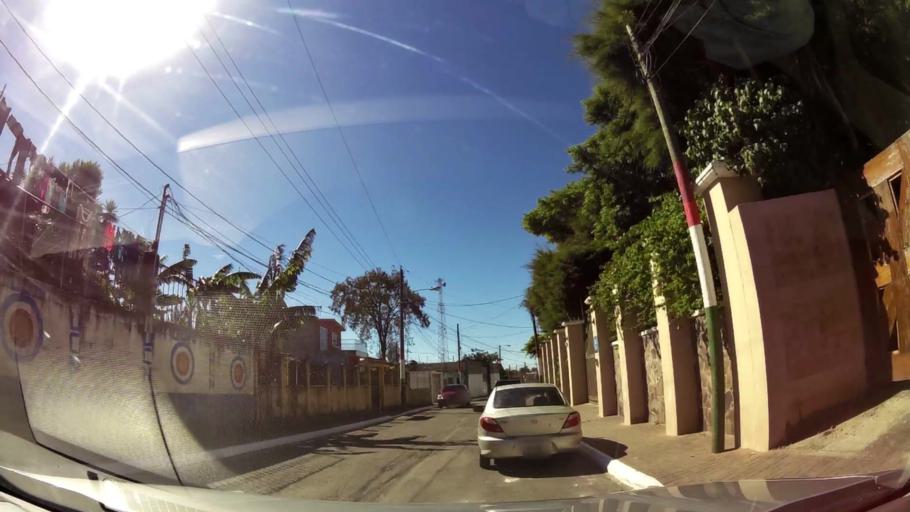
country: GT
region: Guatemala
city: Fraijanes
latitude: 14.4587
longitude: -90.4411
